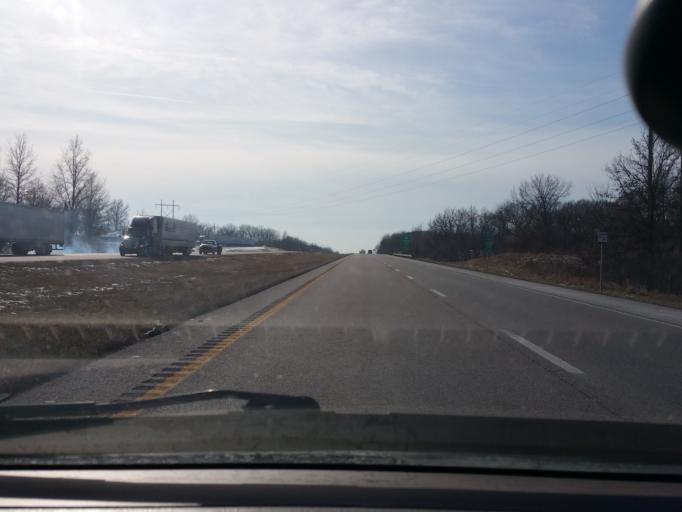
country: US
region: Missouri
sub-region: Clinton County
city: Lathrop
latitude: 39.4777
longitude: -94.3098
